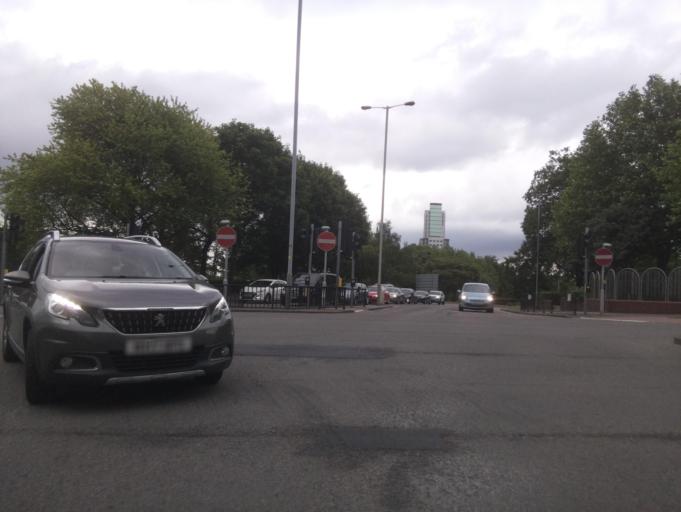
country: GB
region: England
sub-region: Wolverhampton
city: Wolverhampton
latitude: 52.5891
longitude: -2.1266
